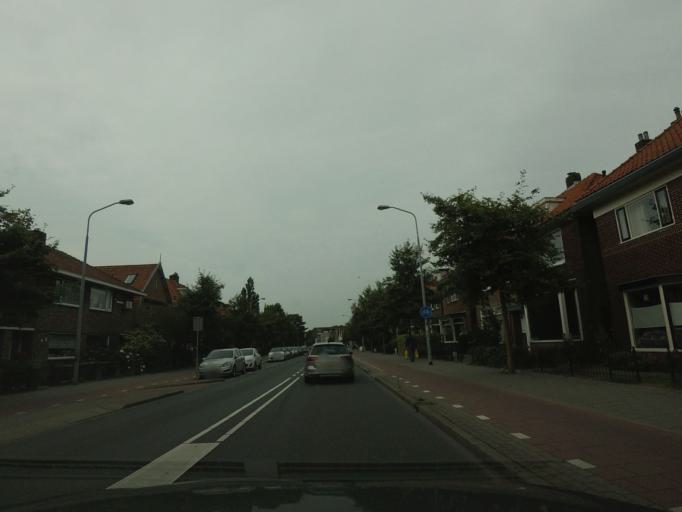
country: NL
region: North Holland
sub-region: Gemeente Zaanstad
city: Zaanstad
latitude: 52.4853
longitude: 4.8056
